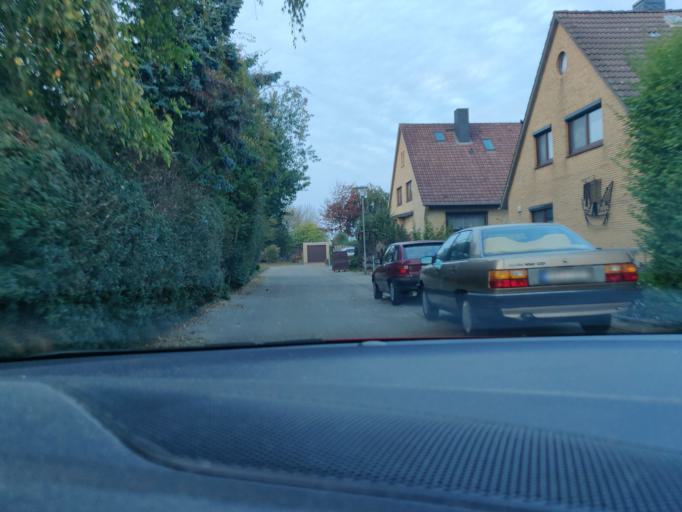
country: DE
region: Lower Saxony
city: Cuxhaven
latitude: 53.8879
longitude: 8.6646
